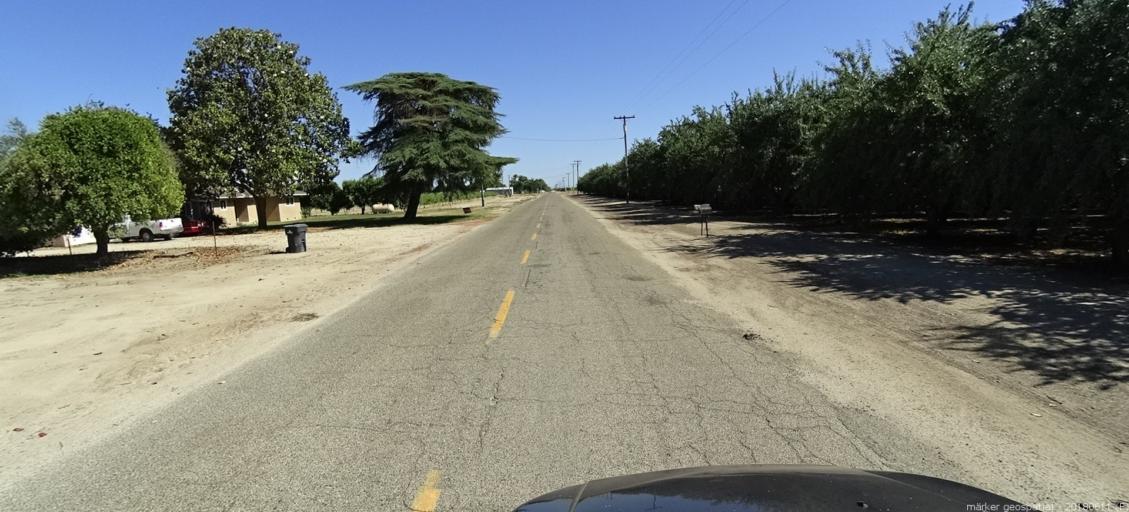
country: US
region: California
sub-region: Madera County
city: Madera
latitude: 36.9472
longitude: -120.1561
